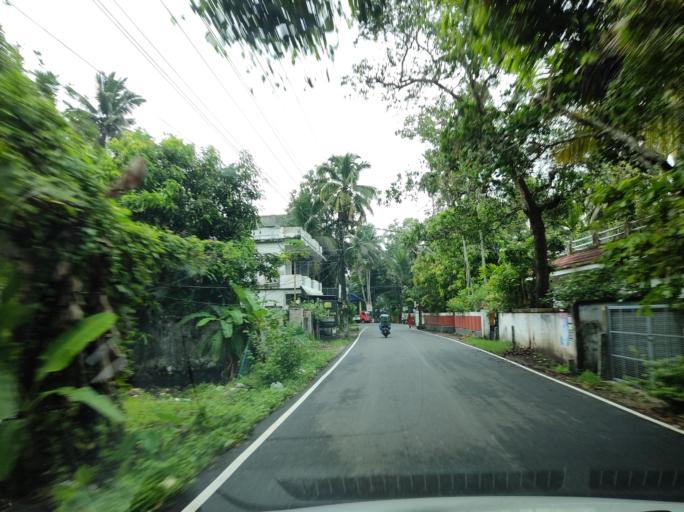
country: IN
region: Kerala
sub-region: Alappuzha
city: Kayankulam
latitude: 9.2619
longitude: 76.4083
